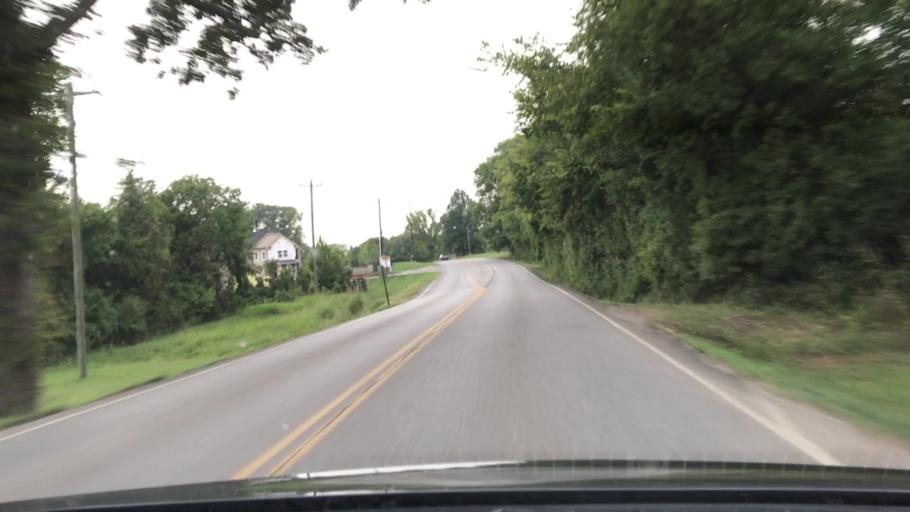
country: US
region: Tennessee
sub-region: Williamson County
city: Nolensville
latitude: 35.9510
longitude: -86.6496
